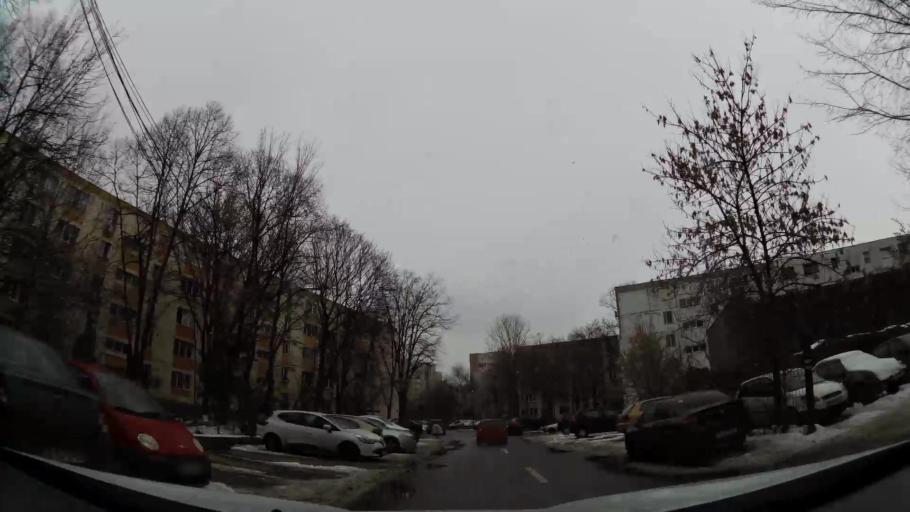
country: RO
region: Ilfov
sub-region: Comuna Chiajna
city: Rosu
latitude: 44.4186
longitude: 26.0266
